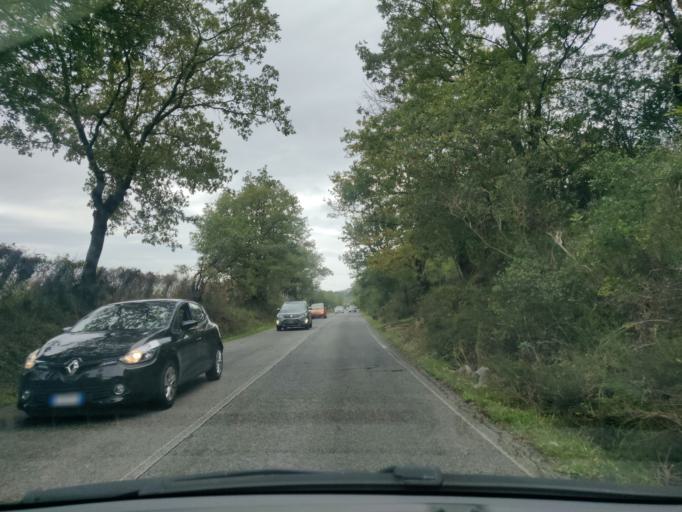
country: IT
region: Latium
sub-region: Citta metropolitana di Roma Capitale
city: Allumiere
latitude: 42.1281
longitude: 11.8658
